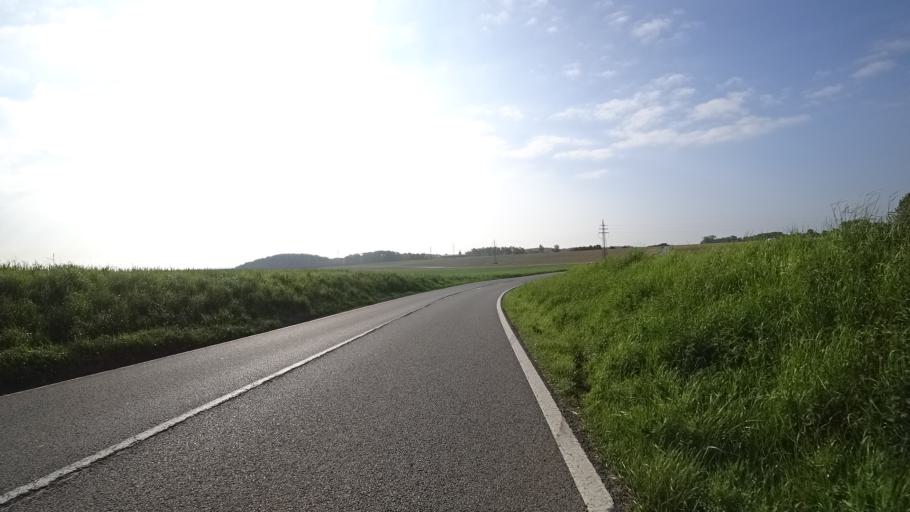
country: BE
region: Wallonia
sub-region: Province de Namur
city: Namur
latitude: 50.5027
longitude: 4.8513
